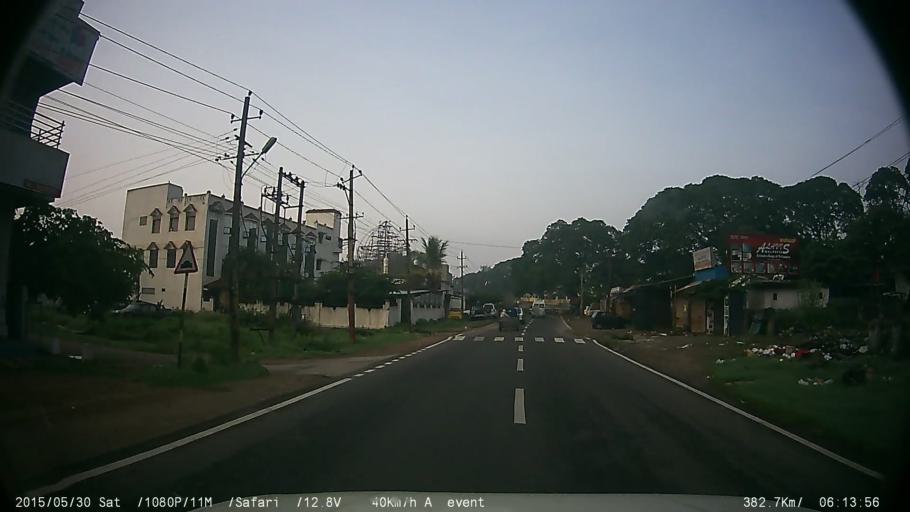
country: IN
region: Karnataka
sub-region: Mysore
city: Mysore
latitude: 12.3309
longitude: 76.6577
